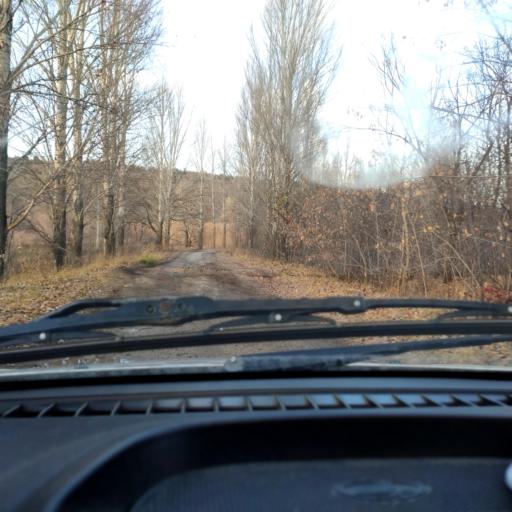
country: RU
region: Samara
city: Povolzhskiy
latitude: 53.4667
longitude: 49.6861
